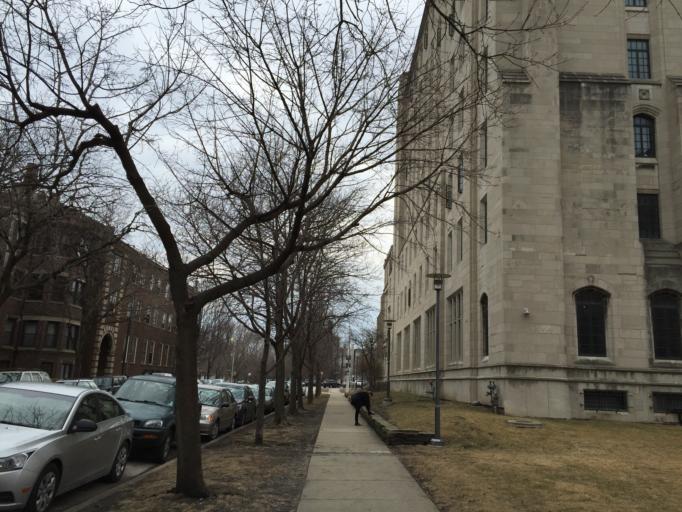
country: US
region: Illinois
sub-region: Cook County
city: Chicago
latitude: 41.7887
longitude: -87.5903
